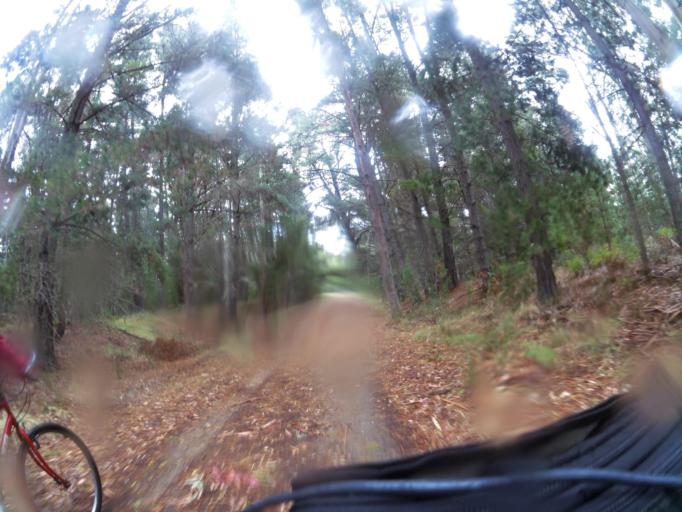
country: AU
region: New South Wales
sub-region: Greater Hume Shire
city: Holbrook
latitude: -36.1888
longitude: 147.5443
